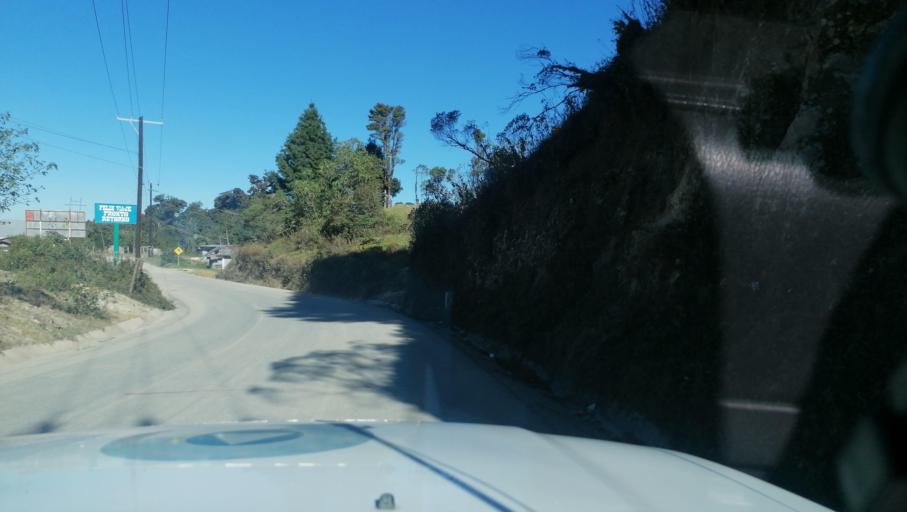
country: MX
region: Chiapas
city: Motozintla de Mendoza
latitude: 15.2627
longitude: -92.2160
